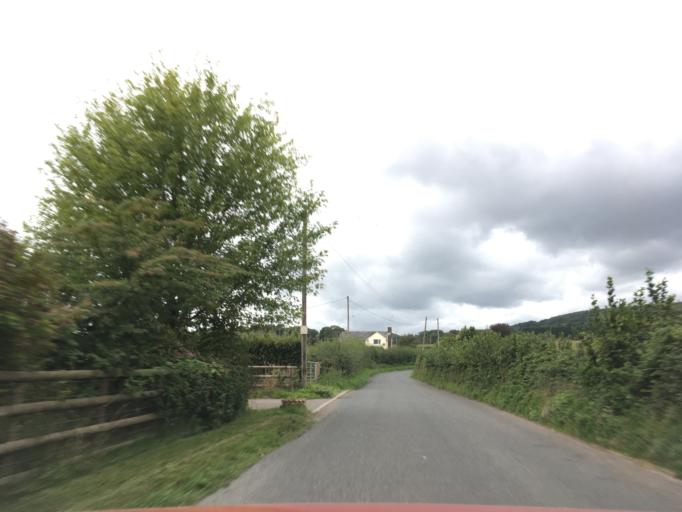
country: GB
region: Wales
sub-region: Newport
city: Llanvaches
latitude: 51.6247
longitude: -2.7911
